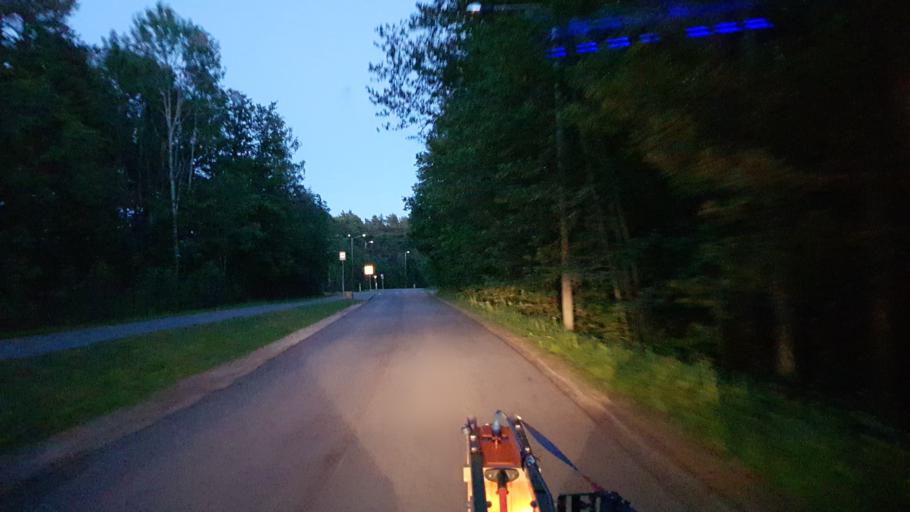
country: EE
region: Harju
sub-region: Harku vald
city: Tabasalu
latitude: 59.4495
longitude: 24.5885
